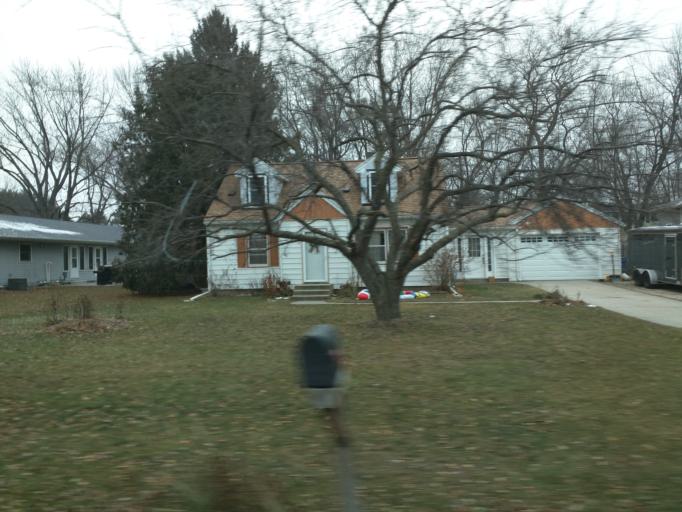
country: US
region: Wisconsin
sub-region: La Crosse County
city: French Island
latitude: 43.8683
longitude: -91.2698
